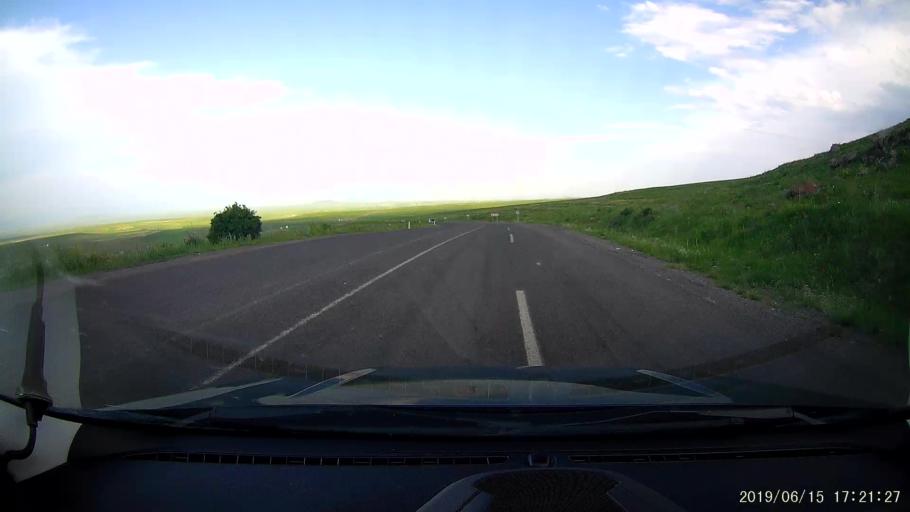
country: TR
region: Kars
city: Basgedikler
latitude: 40.6173
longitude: 43.3249
